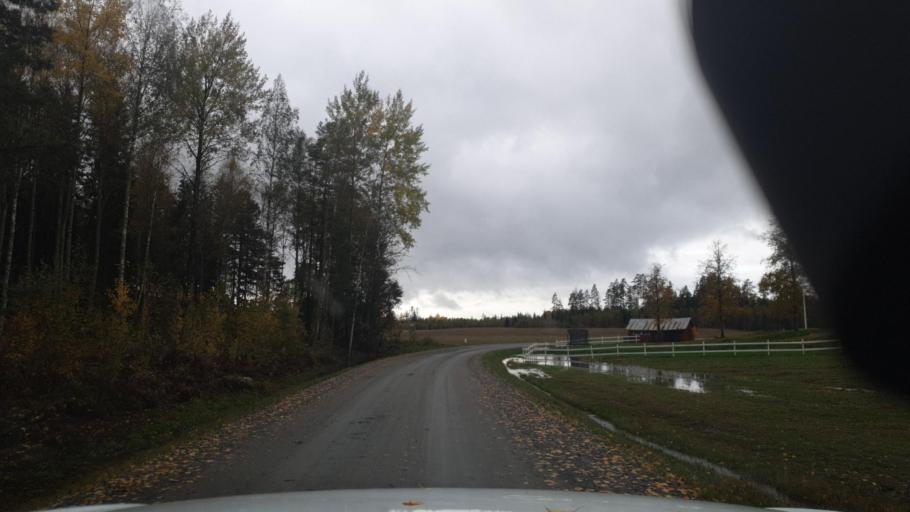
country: SE
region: Vaermland
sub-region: Karlstads Kommun
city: Edsvalla
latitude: 59.4485
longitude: 13.1221
